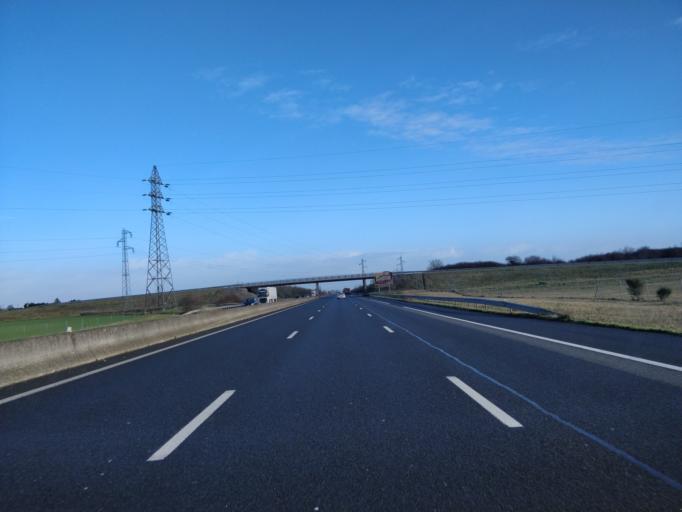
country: FR
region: Centre
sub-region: Departement du Loiret
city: Beaugency
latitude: 47.7913
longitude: 1.6048
